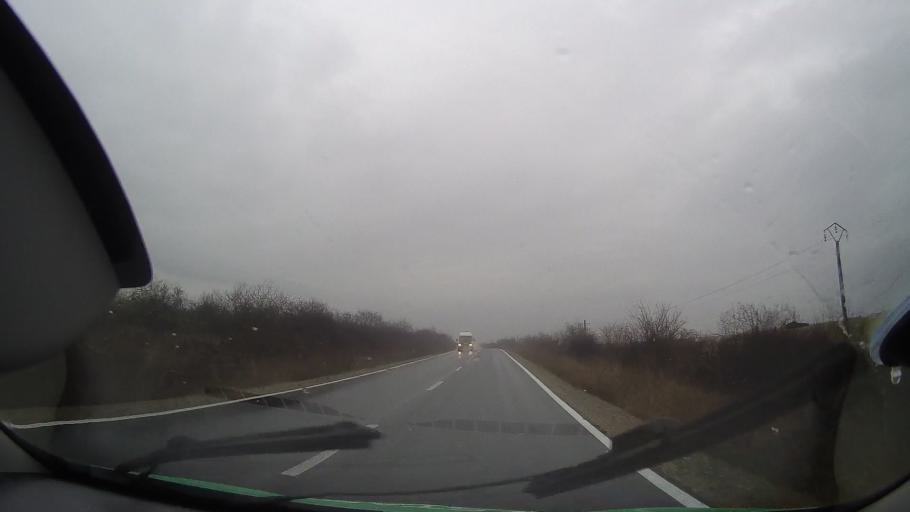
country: RO
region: Bihor
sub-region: Comuna Olcea
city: Olcea
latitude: 46.7065
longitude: 21.9622
